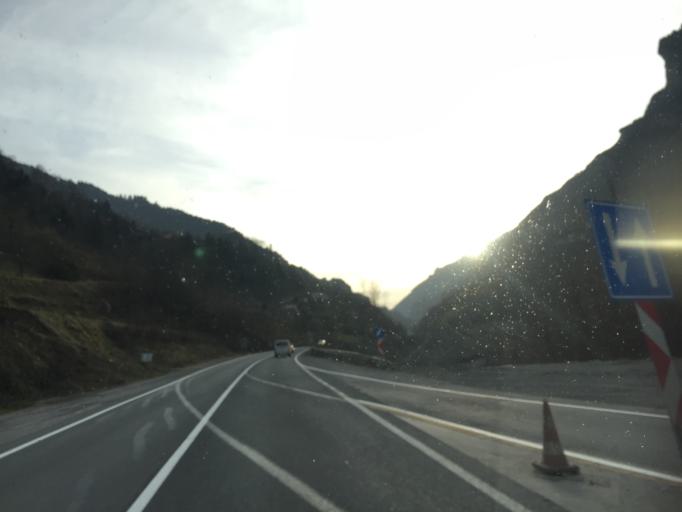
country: TR
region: Trabzon
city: Macka
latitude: 40.7460
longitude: 39.5603
